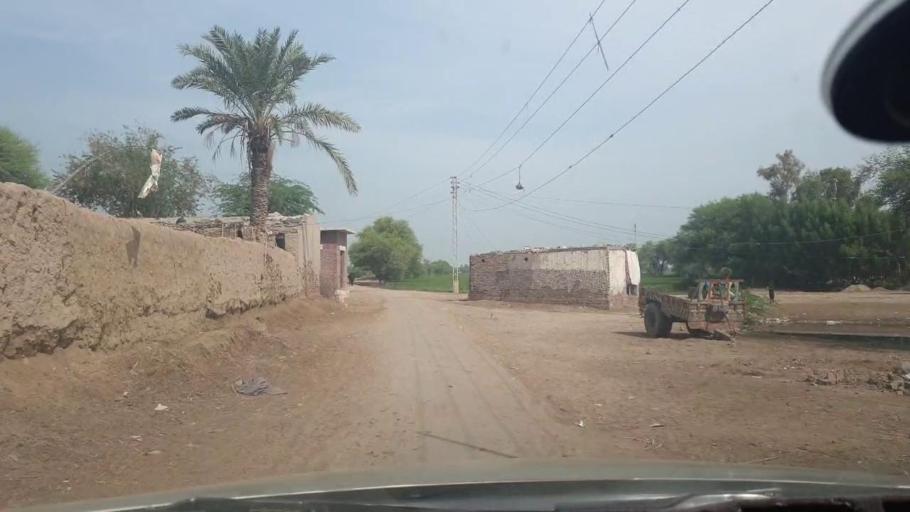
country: PK
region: Sindh
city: Jacobabad
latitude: 28.2974
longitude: 68.4770
